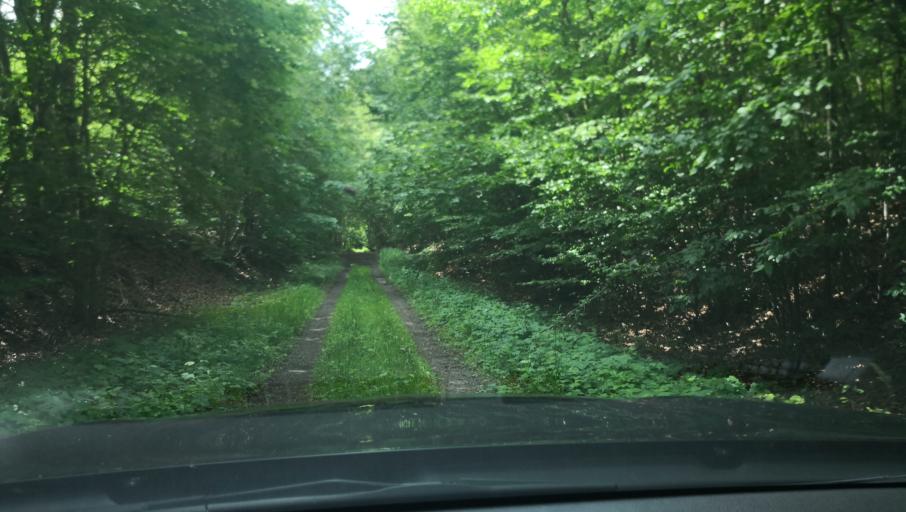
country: SE
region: Skane
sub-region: Tomelilla Kommun
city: Tomelilla
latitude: 55.6112
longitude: 14.1008
